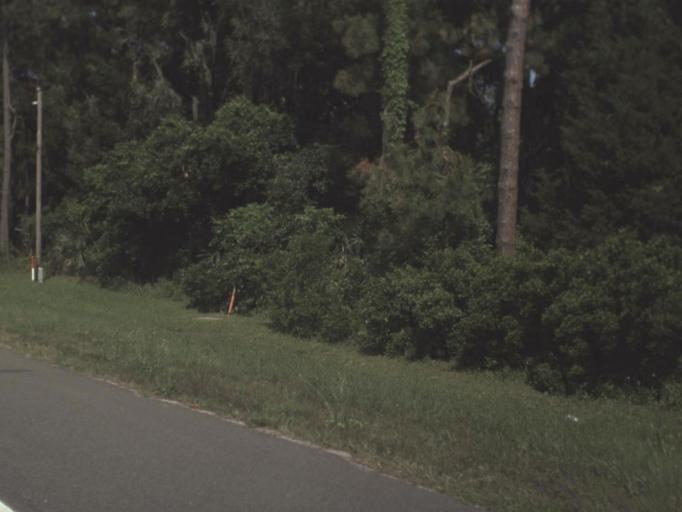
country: US
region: Florida
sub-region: Nassau County
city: Fernandina Beach
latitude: 30.5232
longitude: -81.4438
